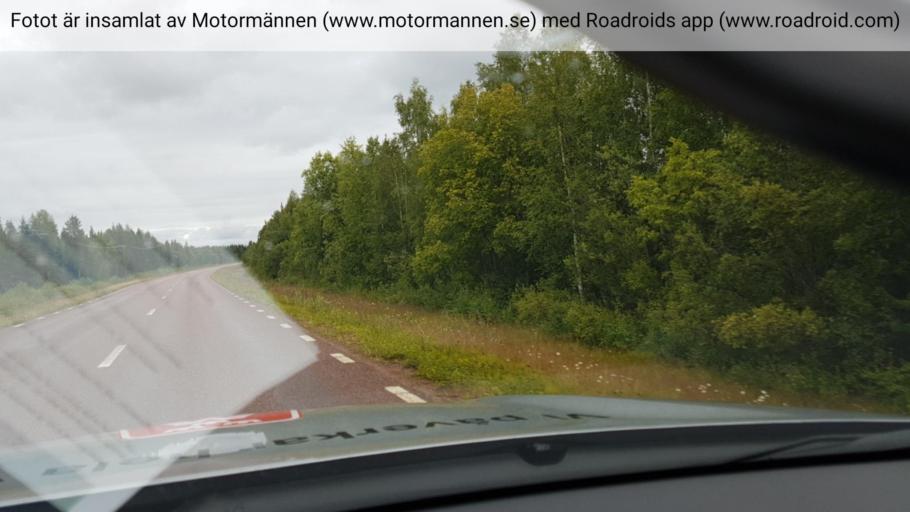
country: SE
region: Norrbotten
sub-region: Pajala Kommun
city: Pajala
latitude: 67.1280
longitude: 22.6066
